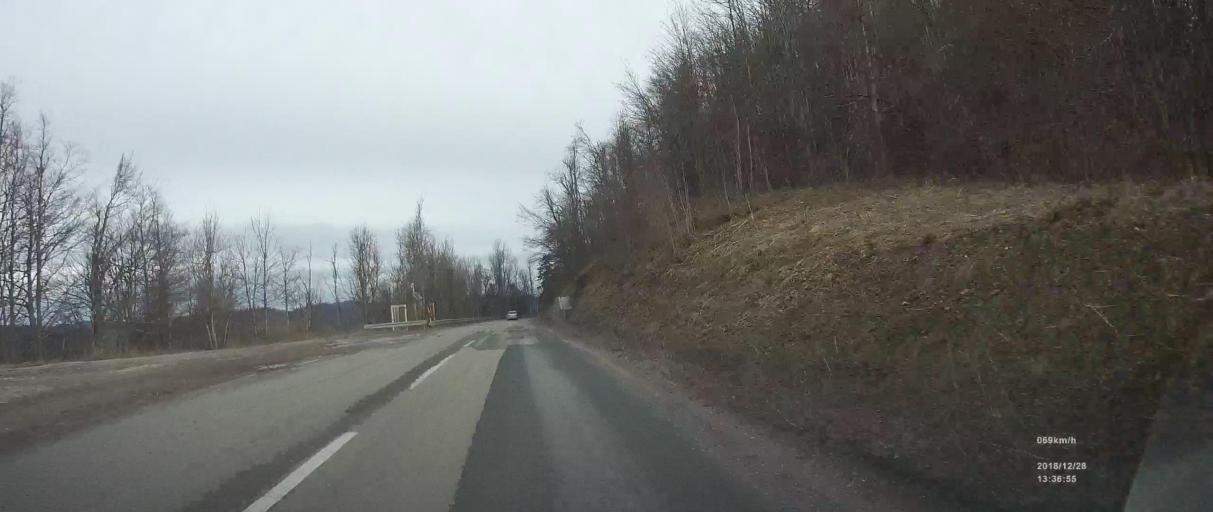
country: HR
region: Primorsko-Goranska
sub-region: Grad Delnice
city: Delnice
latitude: 45.3514
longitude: 14.7095
